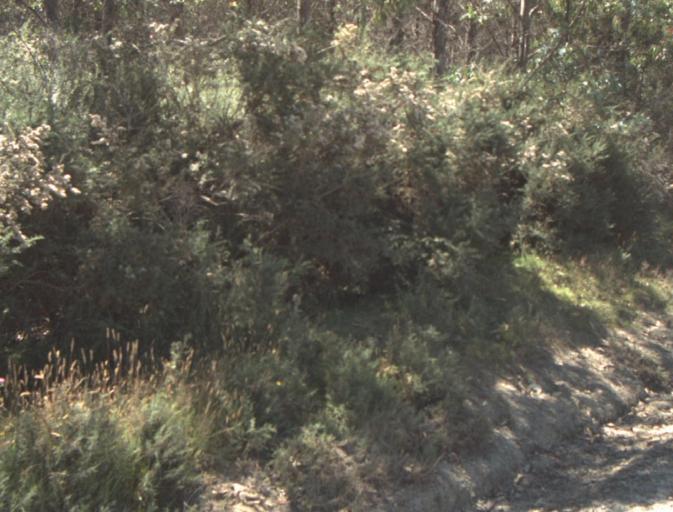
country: AU
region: Tasmania
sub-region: Dorset
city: Scottsdale
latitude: -41.3277
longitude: 147.4859
